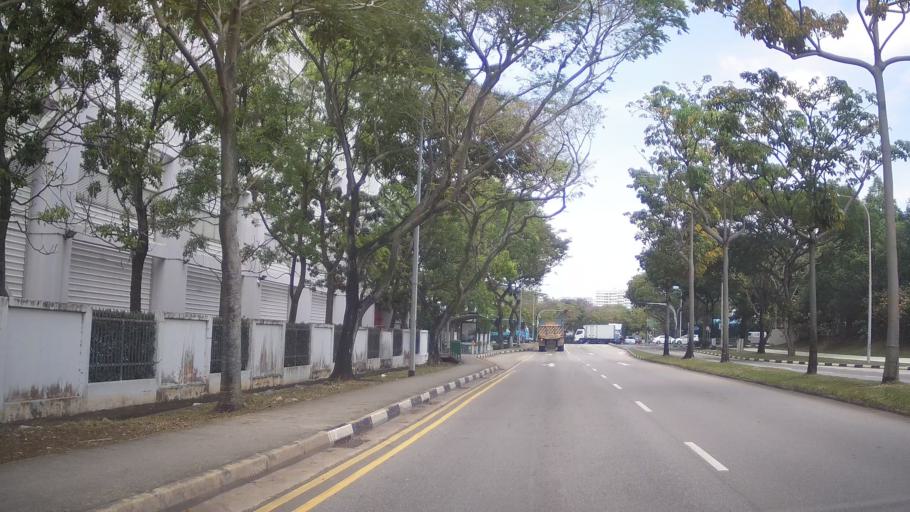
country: MY
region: Johor
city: Johor Bahru
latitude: 1.3364
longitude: 103.7182
